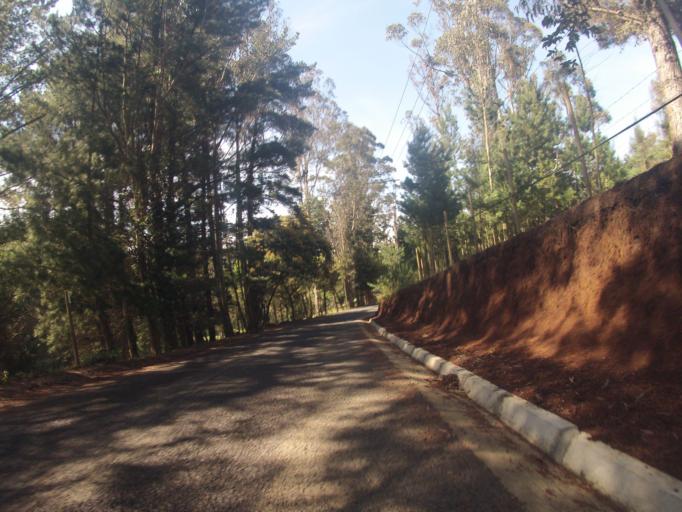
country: CL
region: Araucania
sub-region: Provincia de Cautin
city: Temuco
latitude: -38.6869
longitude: -72.5581
